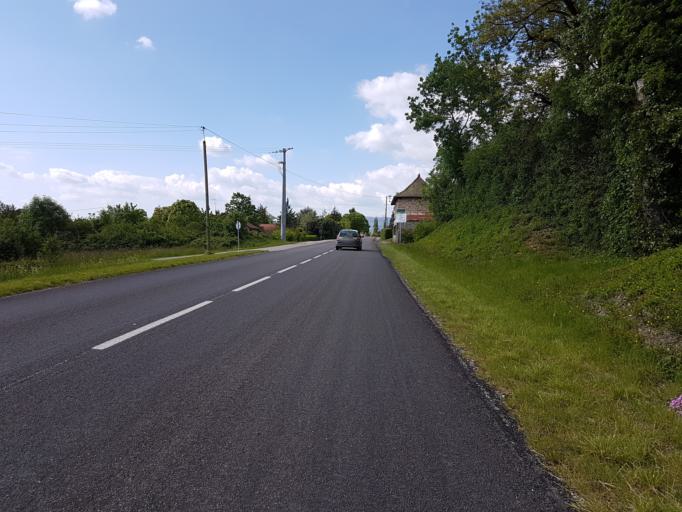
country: FR
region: Rhone-Alpes
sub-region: Departement de l'Isere
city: Bouvesse-Quirieu
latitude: 45.7899
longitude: 5.4623
